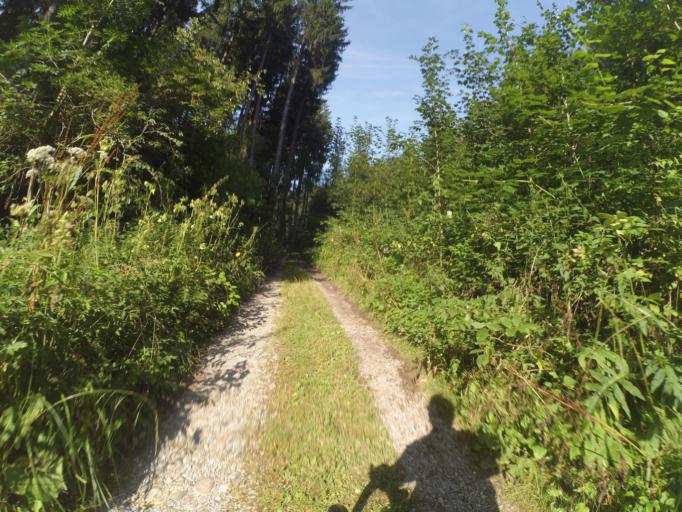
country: DE
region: Bavaria
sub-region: Swabia
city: Unteregg
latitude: 47.9719
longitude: 10.4560
